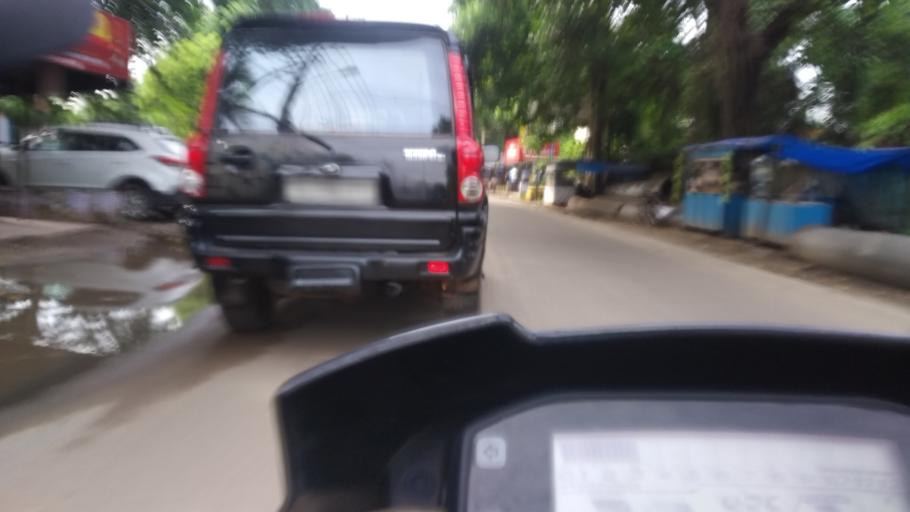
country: IN
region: Kerala
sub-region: Ernakulam
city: Cochin
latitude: 9.9826
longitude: 76.3128
